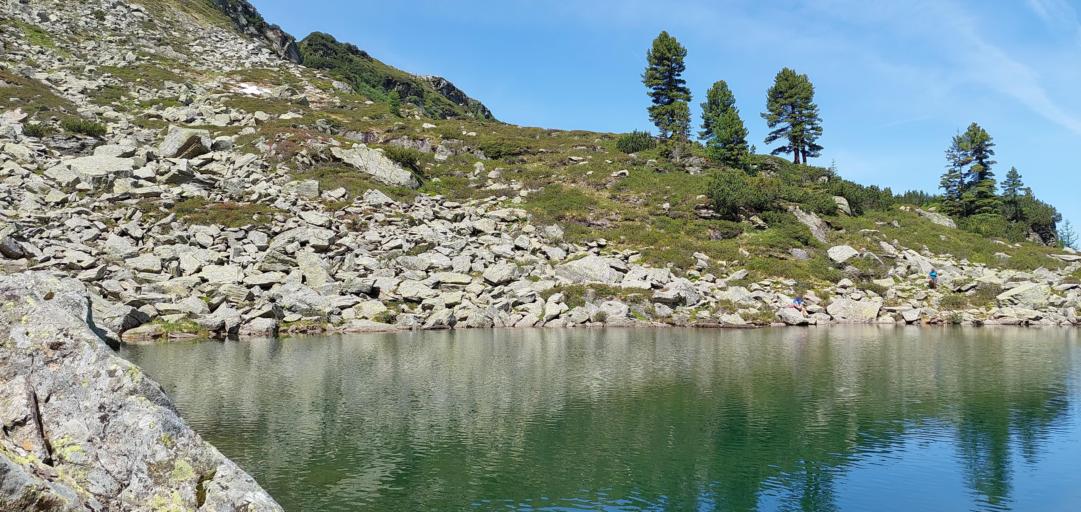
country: AT
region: Salzburg
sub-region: Politischer Bezirk Sankt Johann im Pongau
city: Forstau
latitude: 47.3430
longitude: 13.6022
